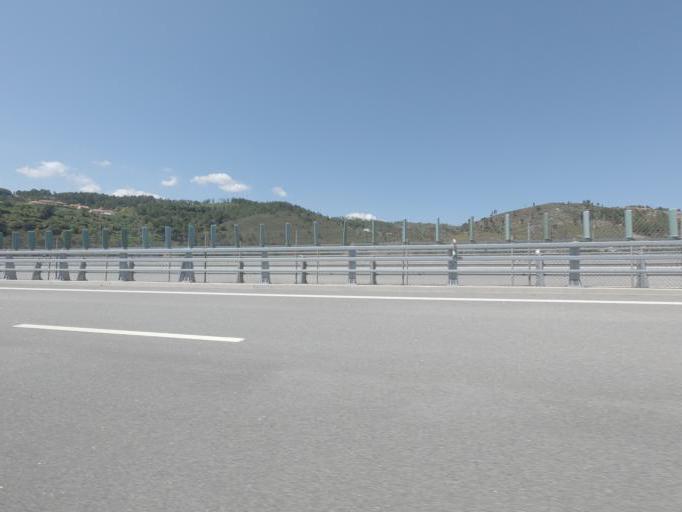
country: PT
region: Porto
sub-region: Amarante
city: Amarante
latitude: 41.2618
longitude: -8.0258
